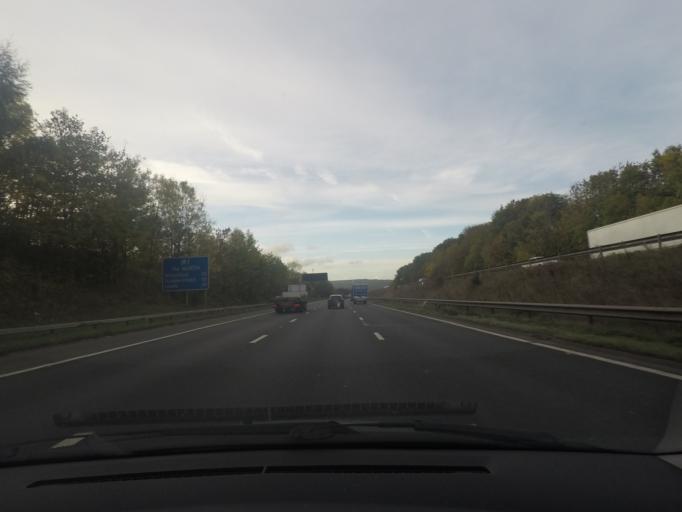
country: GB
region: England
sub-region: Barnsley
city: Dodworth
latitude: 53.5556
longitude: -1.5284
